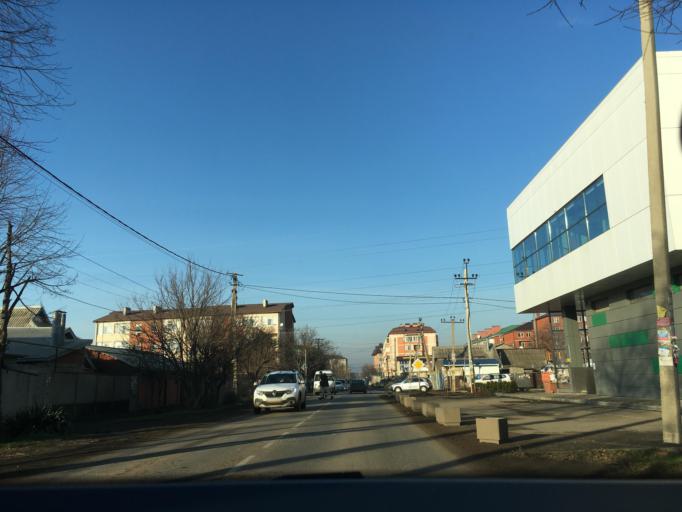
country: RU
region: Krasnodarskiy
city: Krasnodar
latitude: 45.0715
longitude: 39.0214
